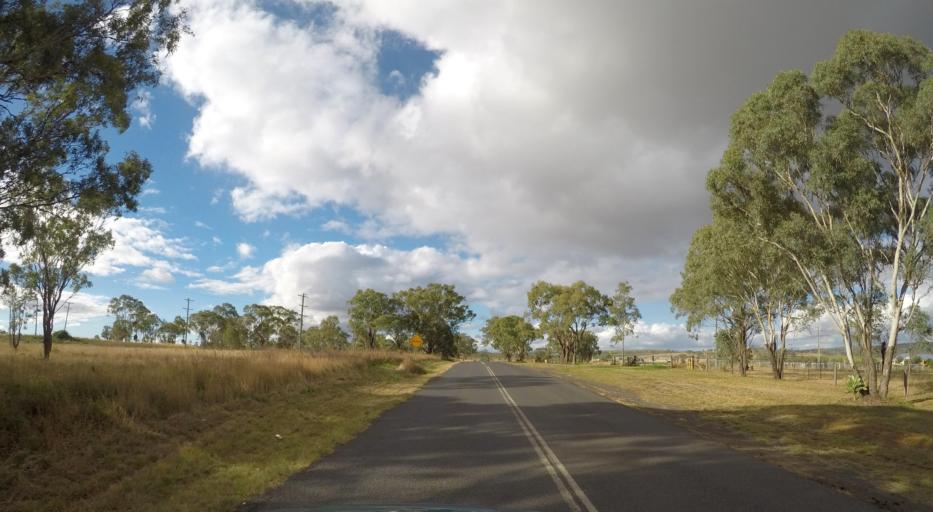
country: AU
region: Queensland
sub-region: Toowoomba
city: Westbrook
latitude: -27.6988
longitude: 151.6644
